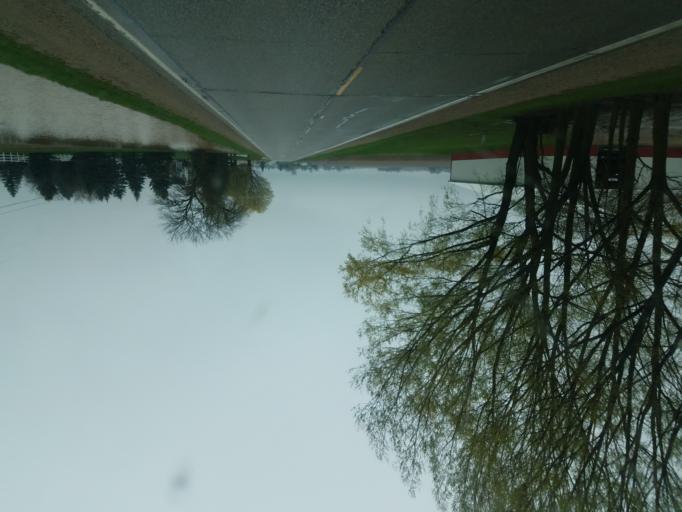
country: US
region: Michigan
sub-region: Isabella County
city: Shepherd
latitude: 43.5242
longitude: -84.7436
